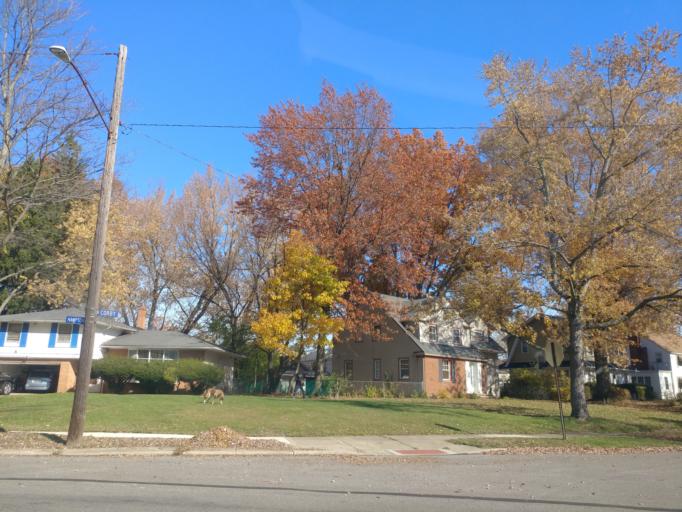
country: US
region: Ohio
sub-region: Cuyahoga County
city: Shaker Heights
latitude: 41.4783
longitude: -81.5880
